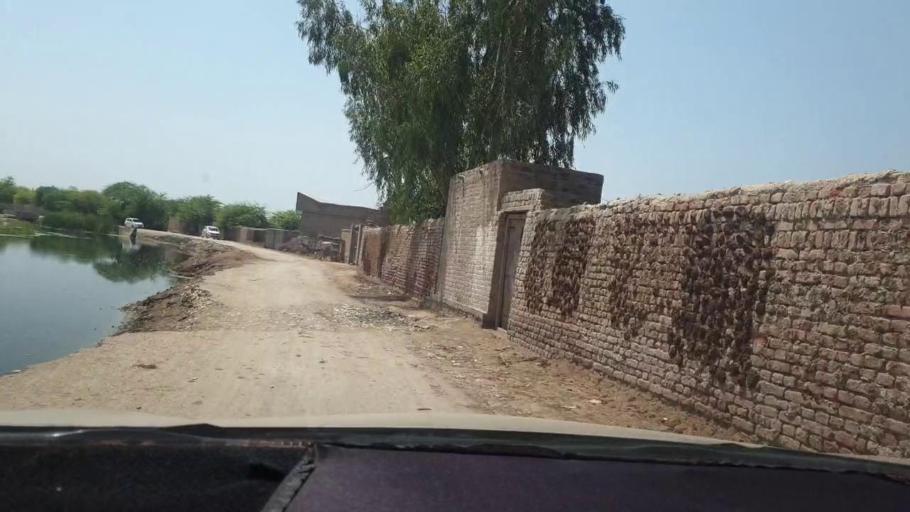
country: PK
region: Sindh
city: Shahdadkot
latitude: 27.8370
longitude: 67.9399
